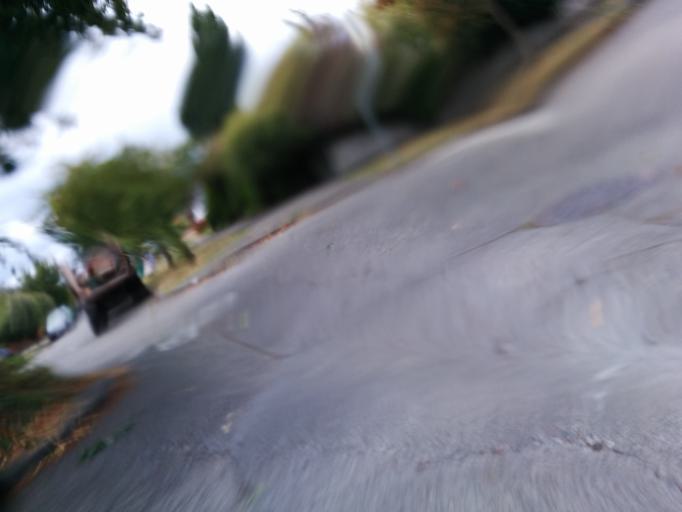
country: US
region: Washington
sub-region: King County
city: Seattle
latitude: 47.6709
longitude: -122.3707
